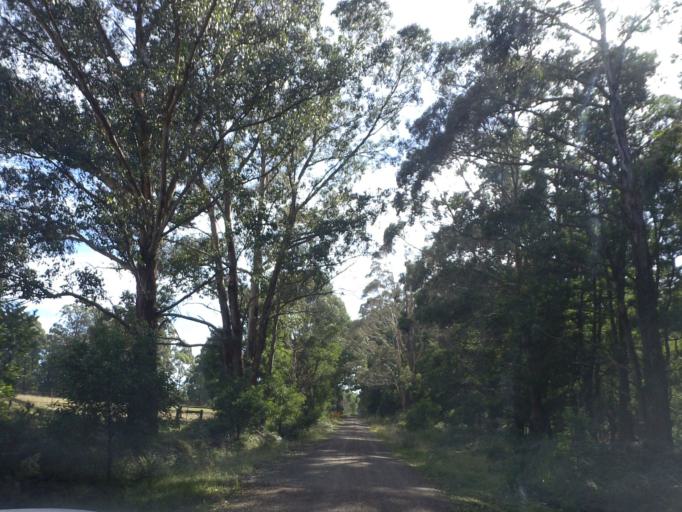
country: AU
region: Victoria
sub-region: Moorabool
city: Bacchus Marsh
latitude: -37.4186
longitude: 144.2490
